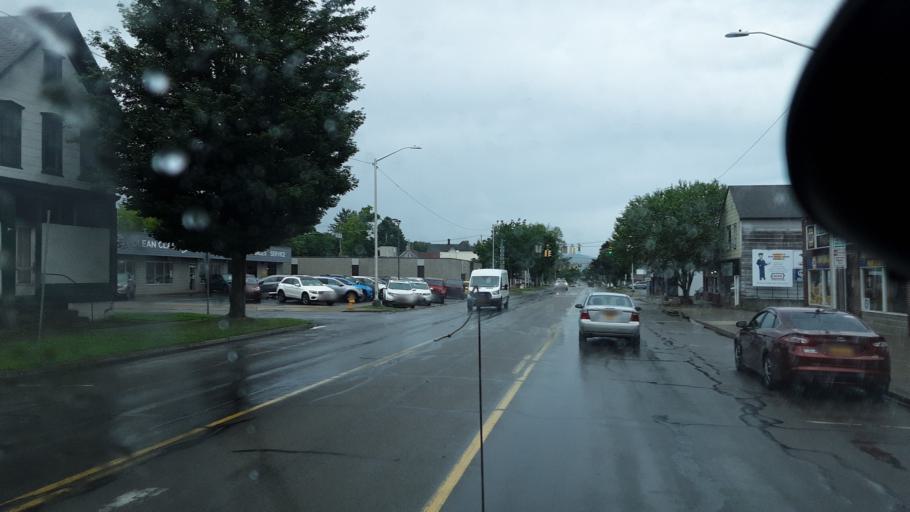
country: US
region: New York
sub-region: Cattaraugus County
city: Olean
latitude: 42.0774
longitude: -78.4435
